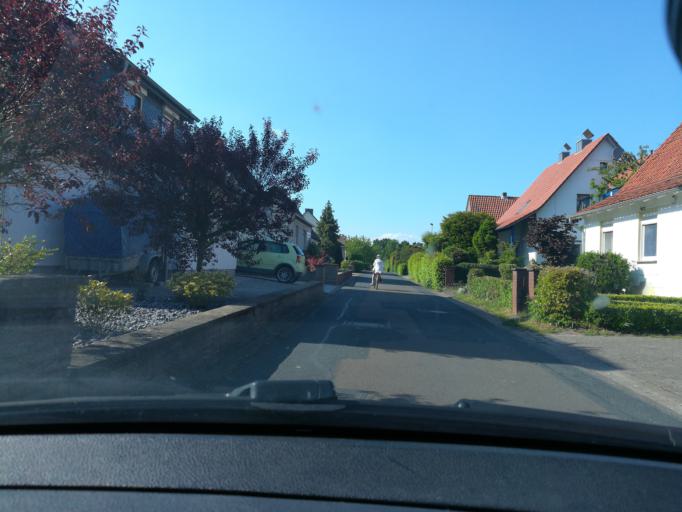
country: DE
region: North Rhine-Westphalia
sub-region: Regierungsbezirk Detmold
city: Minden
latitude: 52.3118
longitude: 8.9316
